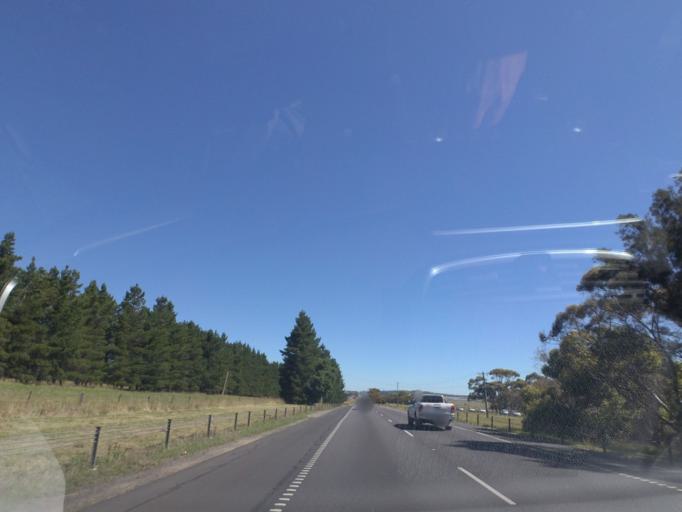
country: AU
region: Victoria
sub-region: Hume
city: Craigieburn
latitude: -37.5148
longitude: 144.9498
